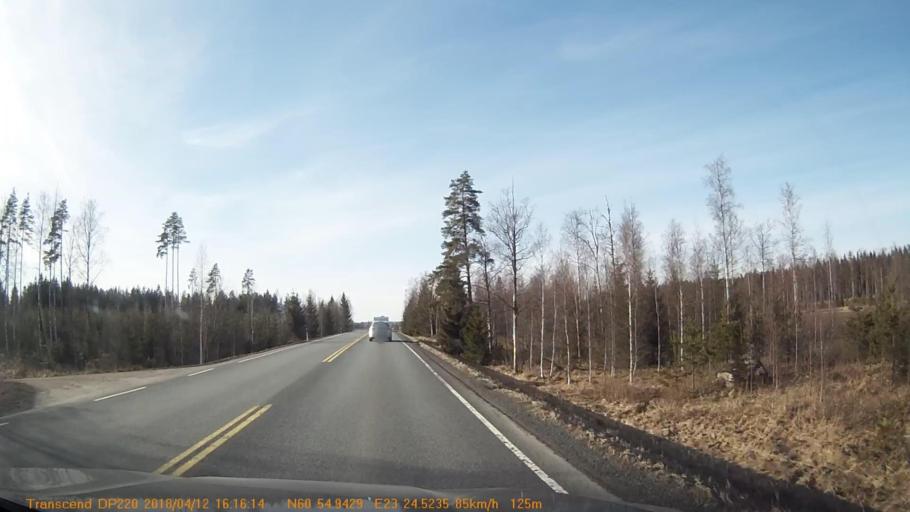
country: FI
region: Haeme
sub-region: Forssa
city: Humppila
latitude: 60.9158
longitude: 23.4086
